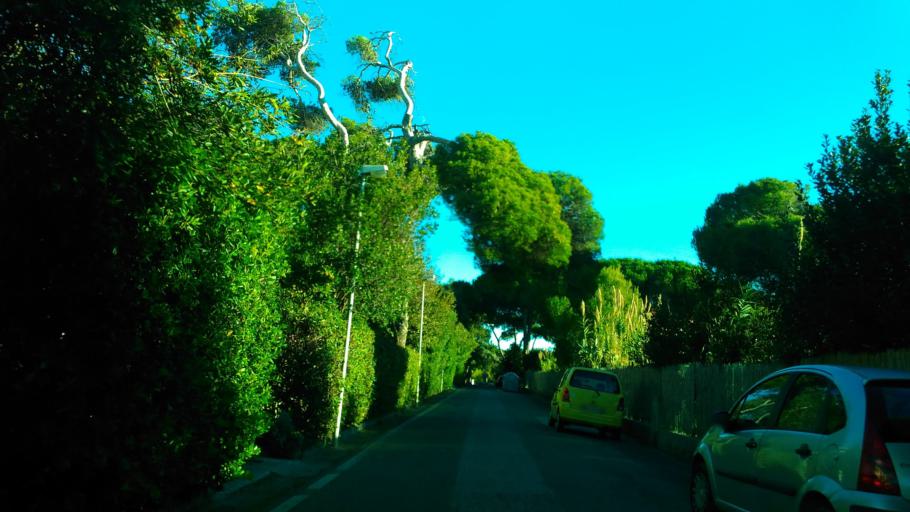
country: IT
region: Tuscany
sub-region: Provincia di Livorno
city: Quercianella
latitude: 43.4582
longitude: 10.3671
